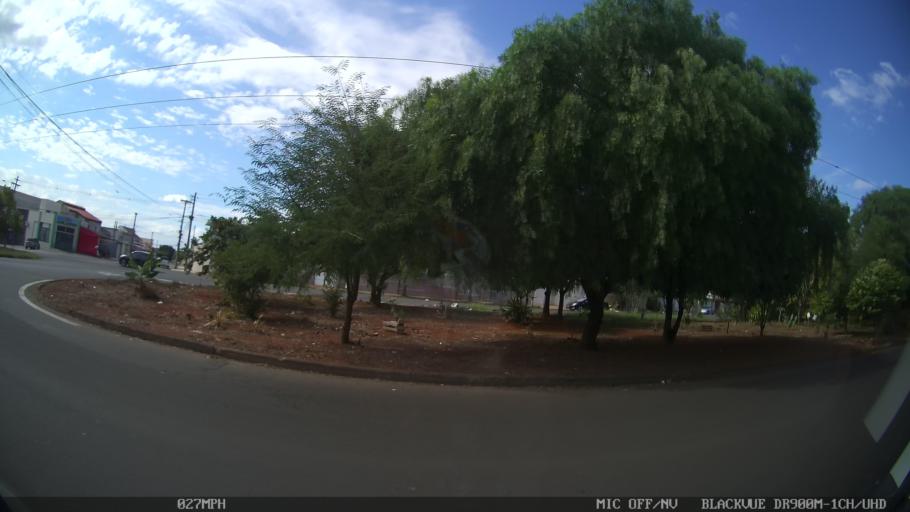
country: BR
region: Sao Paulo
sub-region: Americana
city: Americana
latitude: -22.7186
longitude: -47.3203
